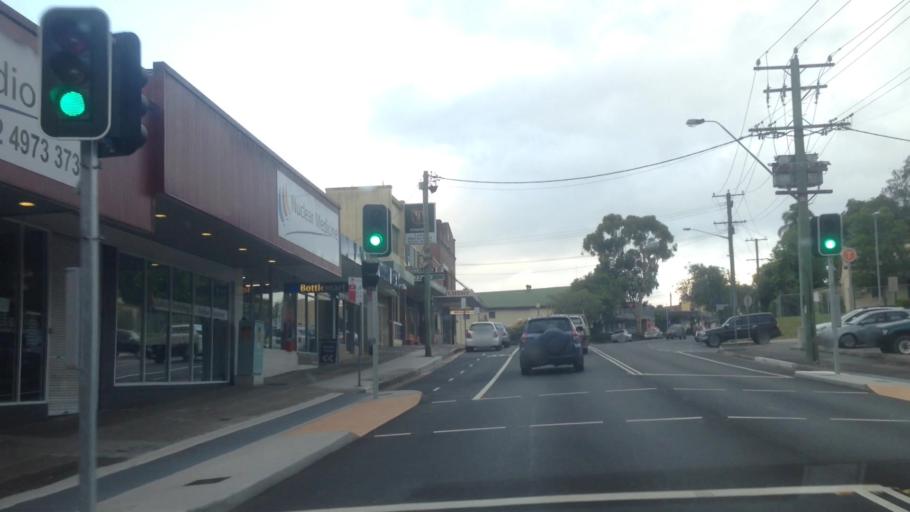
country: AU
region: New South Wales
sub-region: Lake Macquarie Shire
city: Dora Creek
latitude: -33.1089
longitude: 151.4870
